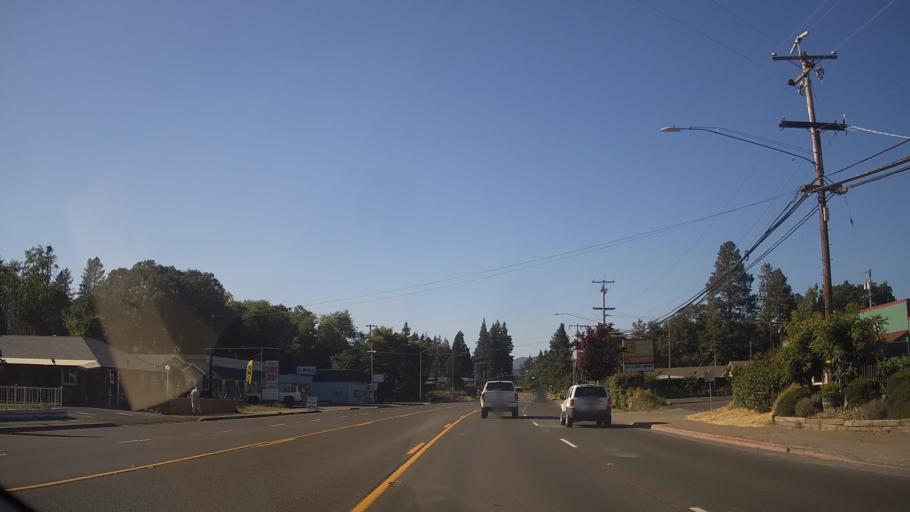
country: US
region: California
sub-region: Mendocino County
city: Willits
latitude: 39.3961
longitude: -123.3493
